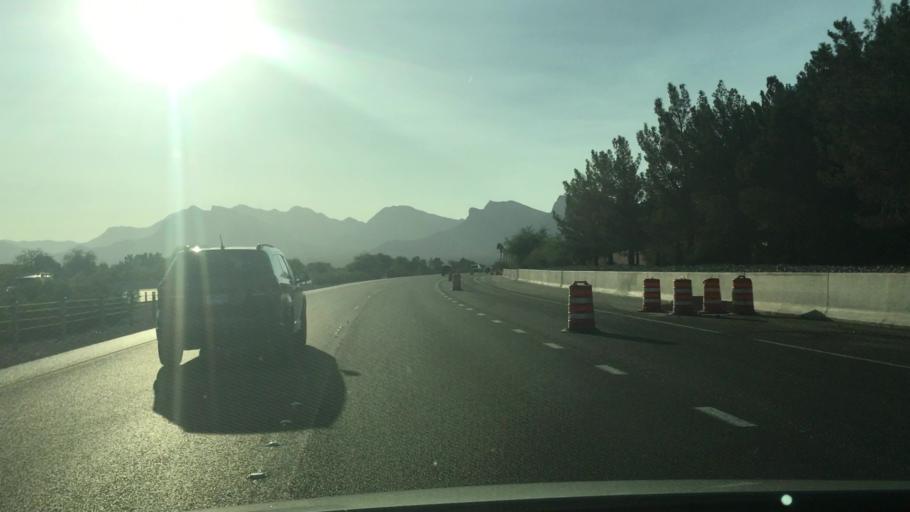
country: US
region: Nevada
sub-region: Clark County
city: Summerlin South
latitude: 36.1789
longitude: -115.2945
